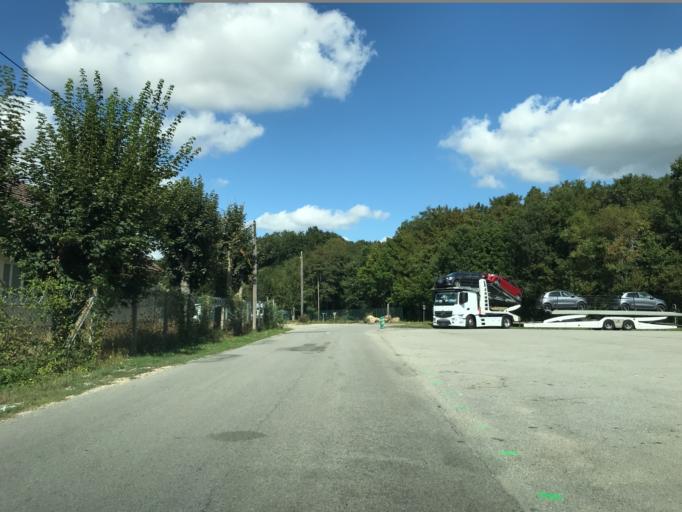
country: FR
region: Haute-Normandie
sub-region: Departement de l'Eure
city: La Chapelle-Reanville
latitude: 49.0943
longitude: 1.3915
